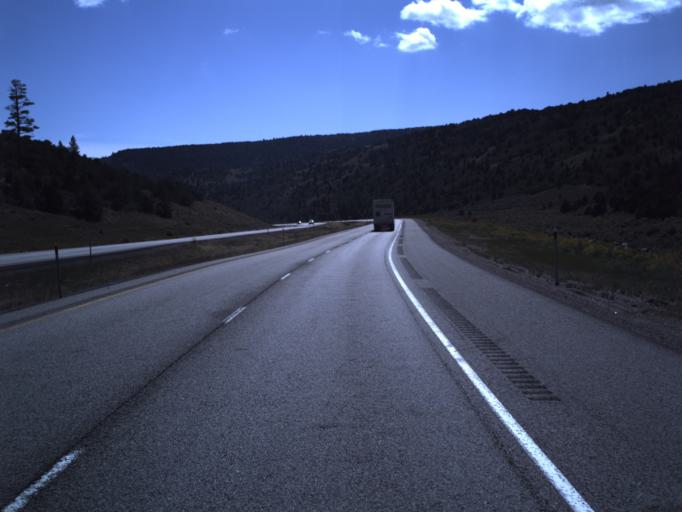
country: US
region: Utah
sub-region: Wayne County
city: Loa
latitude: 38.7720
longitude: -111.4736
